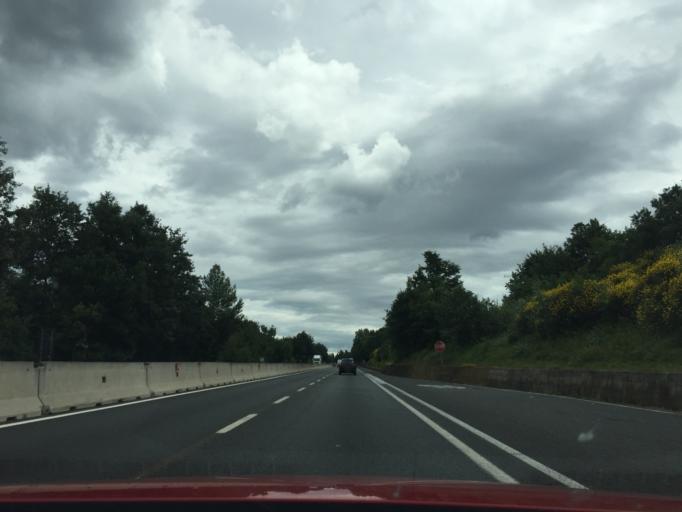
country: IT
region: Tuscany
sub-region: Province of Florence
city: Quattro Strade
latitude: 43.7268
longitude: 11.0923
